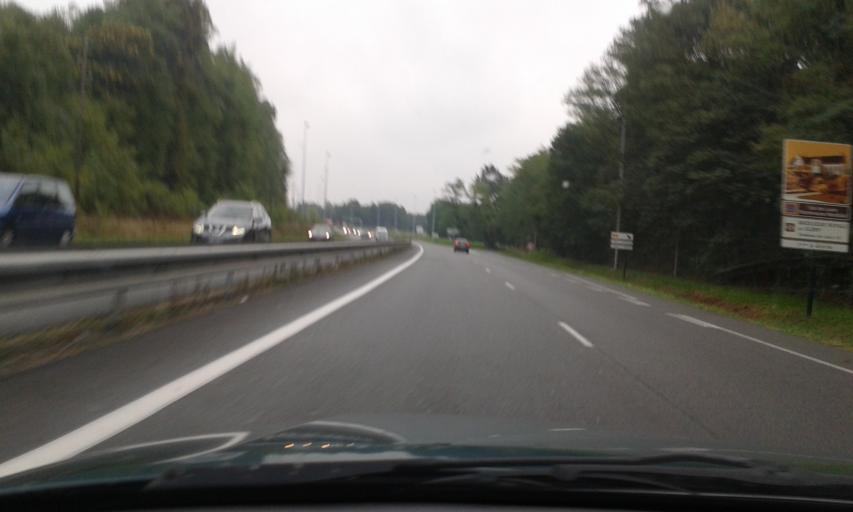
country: FR
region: Centre
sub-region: Departement du Loiret
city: Olivet
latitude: 47.8405
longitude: 1.8710
